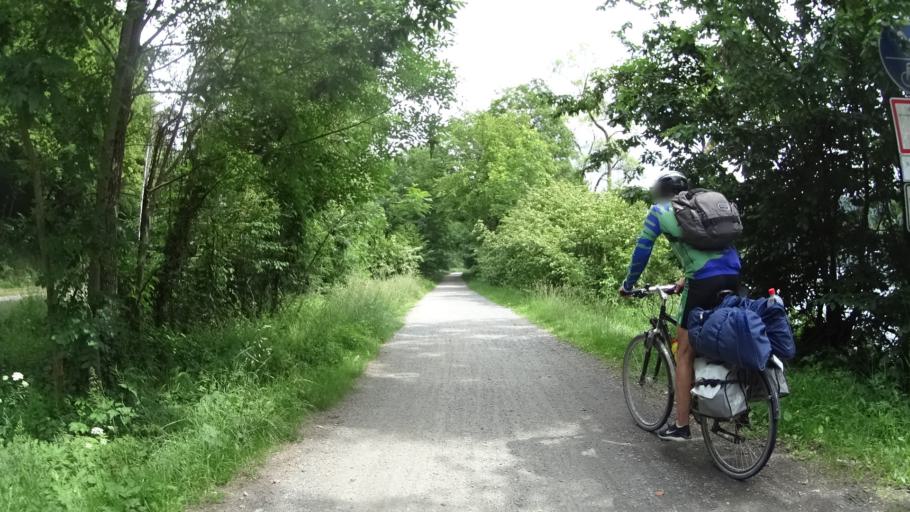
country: DE
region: Bavaria
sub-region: Lower Bavaria
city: Aicha vorm Wald
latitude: 48.6095
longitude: 13.3043
